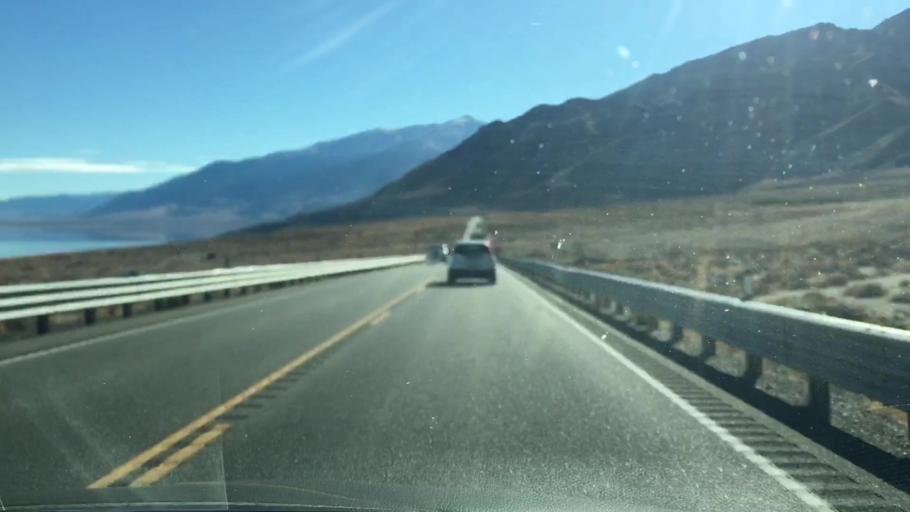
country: US
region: Nevada
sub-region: Mineral County
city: Hawthorne
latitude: 38.7436
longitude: -118.7673
